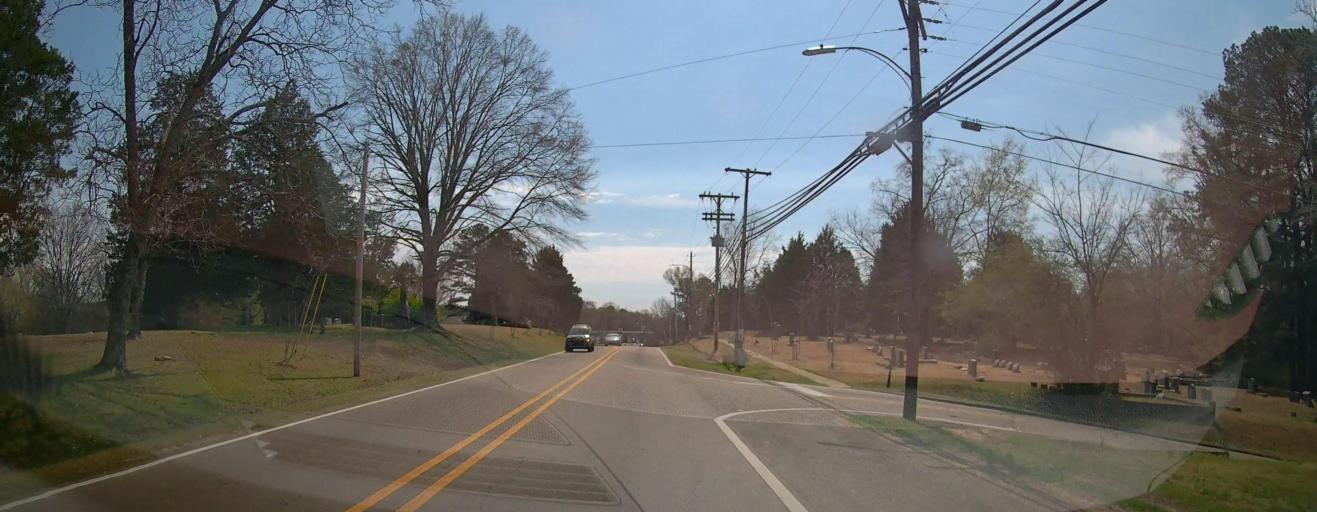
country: US
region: Mississippi
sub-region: Union County
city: New Albany
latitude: 34.4854
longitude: -89.0014
